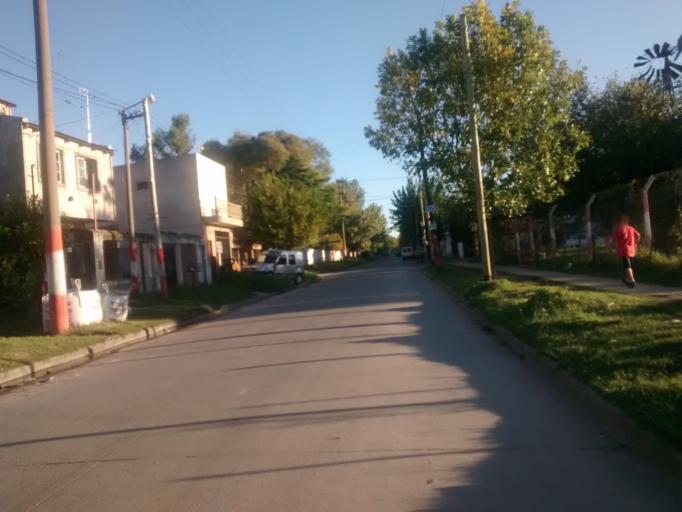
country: AR
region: Buenos Aires
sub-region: Partido de La Plata
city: La Plata
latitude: -34.9064
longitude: -57.9187
